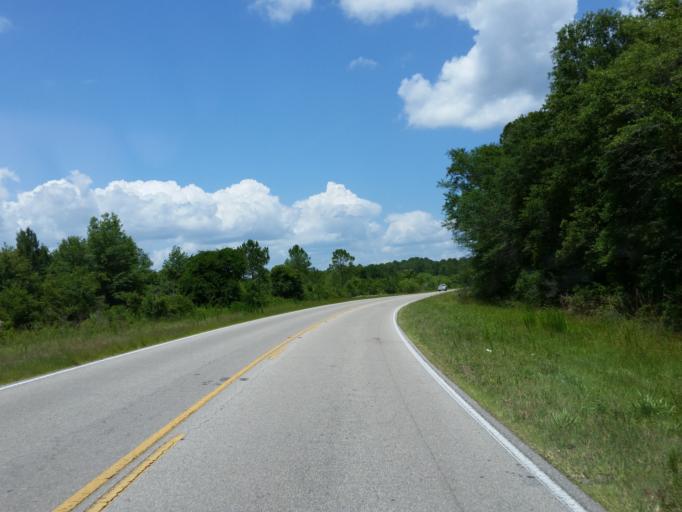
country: US
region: Florida
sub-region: Alachua County
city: Gainesville
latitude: 29.5084
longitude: -82.2922
